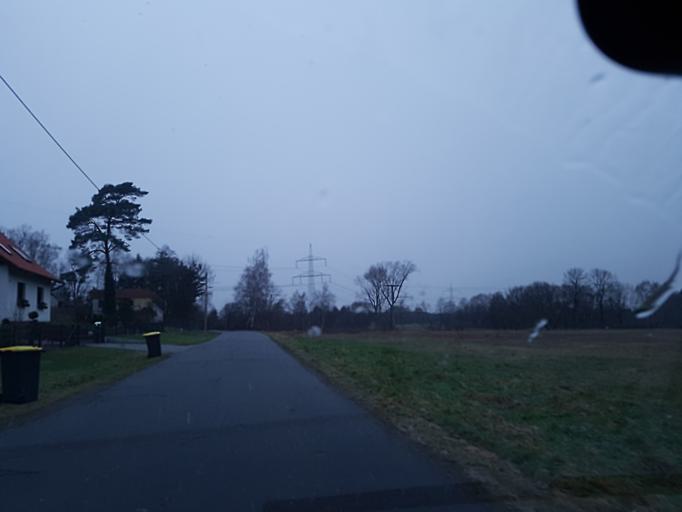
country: DE
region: Brandenburg
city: Bad Liebenwerda
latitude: 51.5356
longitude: 13.4220
